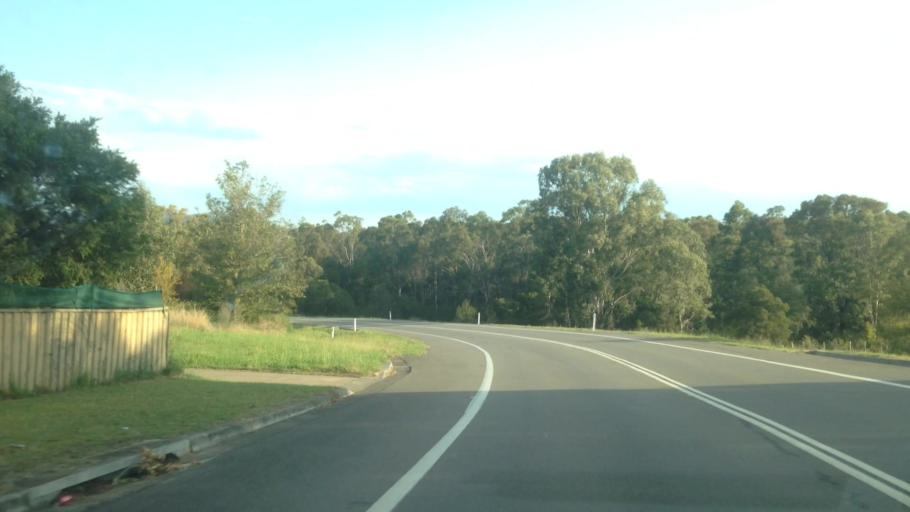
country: AU
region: New South Wales
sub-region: Cessnock
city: Kurri Kurri
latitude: -32.8335
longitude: 151.4804
